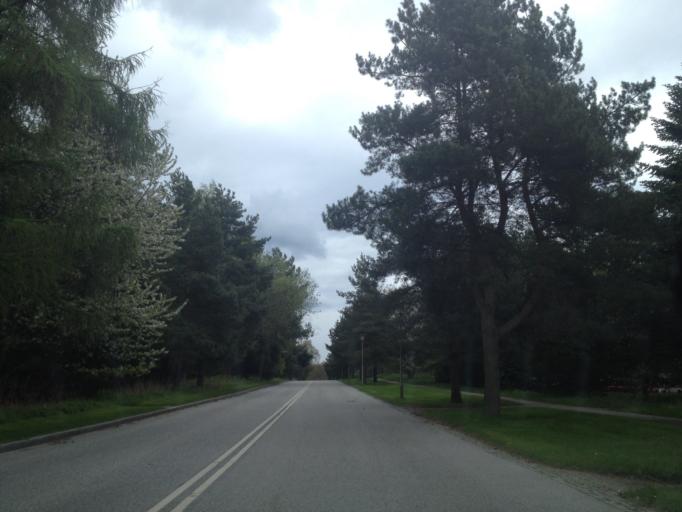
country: DK
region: Capital Region
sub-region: Horsholm Kommune
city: Horsholm
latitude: 55.8684
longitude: 12.4933
